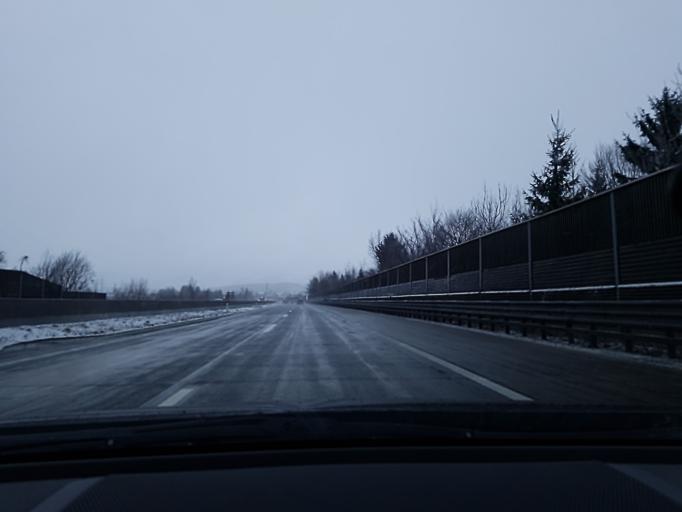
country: AT
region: Salzburg
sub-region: Politischer Bezirk Hallein
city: Kuchl
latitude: 47.6367
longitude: 13.1342
